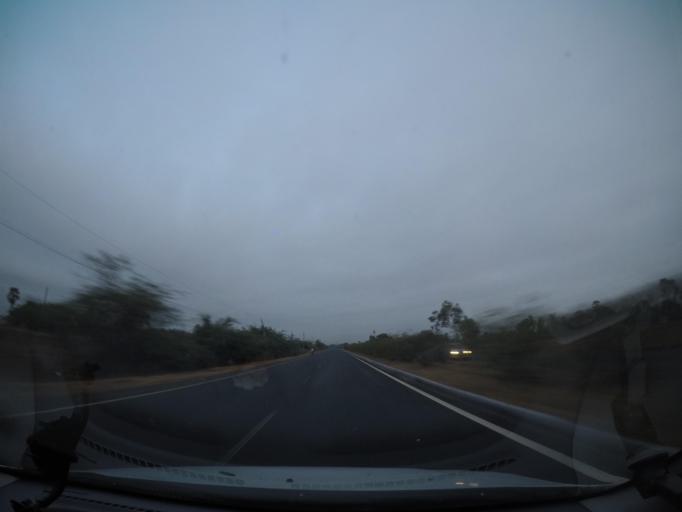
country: IN
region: Andhra Pradesh
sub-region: West Godavari
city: Tadepallegudem
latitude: 16.8100
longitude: 81.3348
